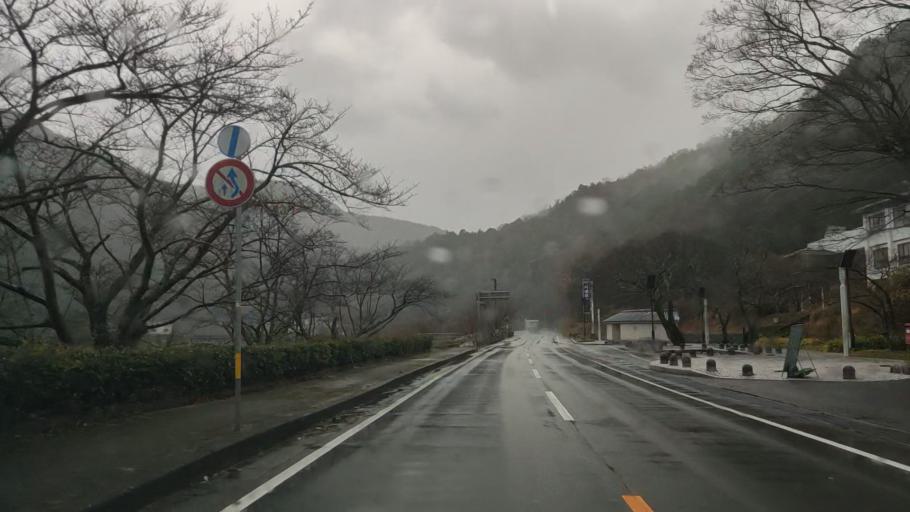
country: JP
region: Tokushima
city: Kamojimacho-jogejima
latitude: 34.1503
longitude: 134.3528
